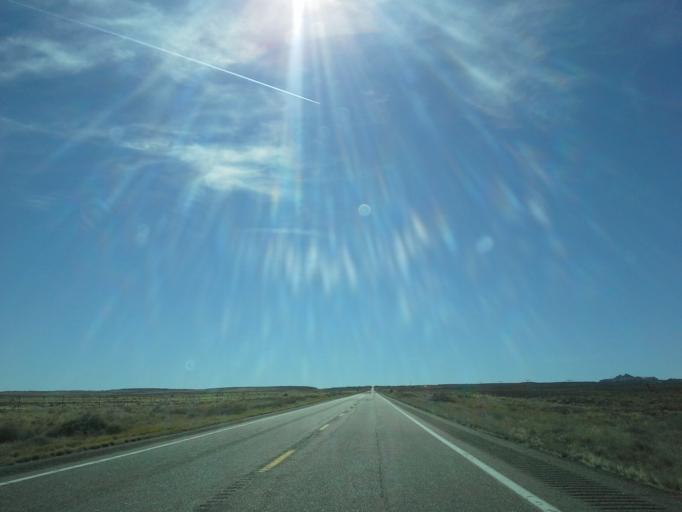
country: US
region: Arizona
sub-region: Coconino County
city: LeChee
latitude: 36.7486
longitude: -111.5757
